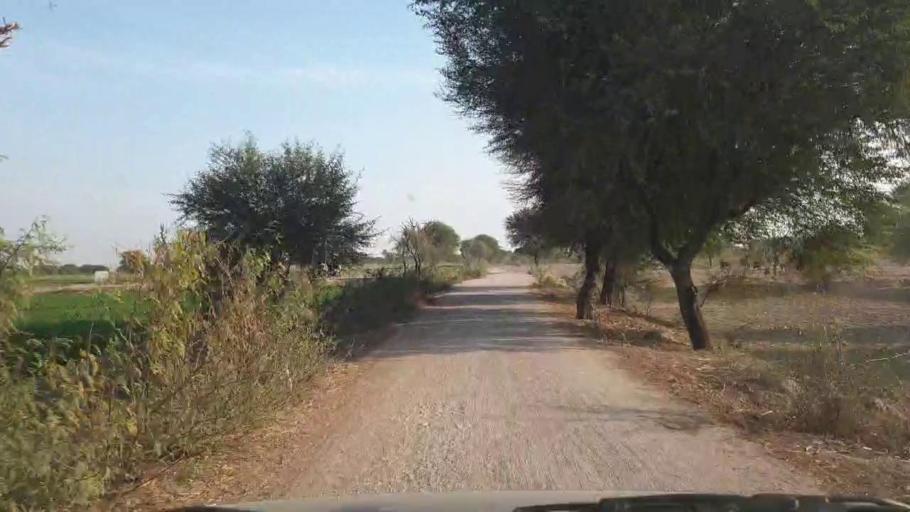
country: PK
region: Sindh
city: Chambar
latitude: 25.2387
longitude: 68.7908
